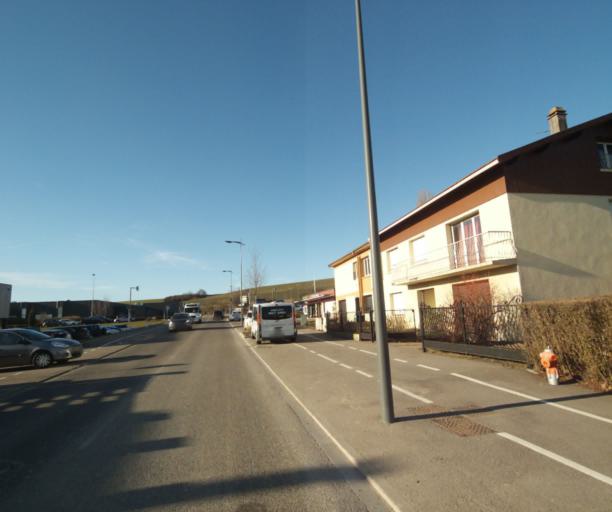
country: FR
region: Lorraine
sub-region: Departement de Meurthe-et-Moselle
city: Seichamps
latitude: 48.7132
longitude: 6.2515
